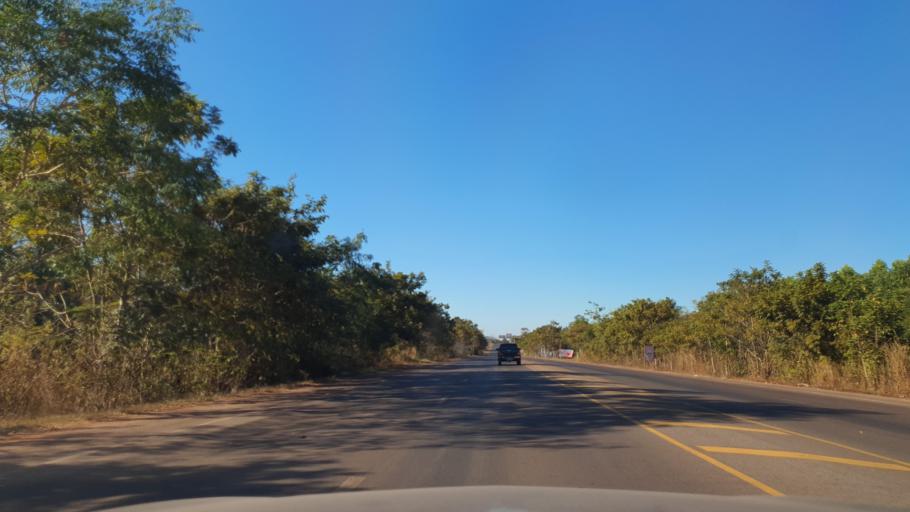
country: TH
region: Nakhon Phanom
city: Si Songkhram
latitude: 17.7686
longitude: 104.2792
